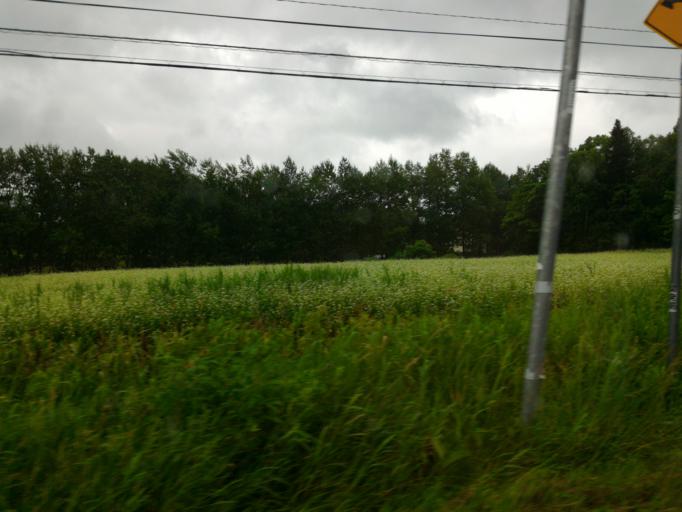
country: JP
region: Hokkaido
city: Nayoro
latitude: 44.6677
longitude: 142.2685
